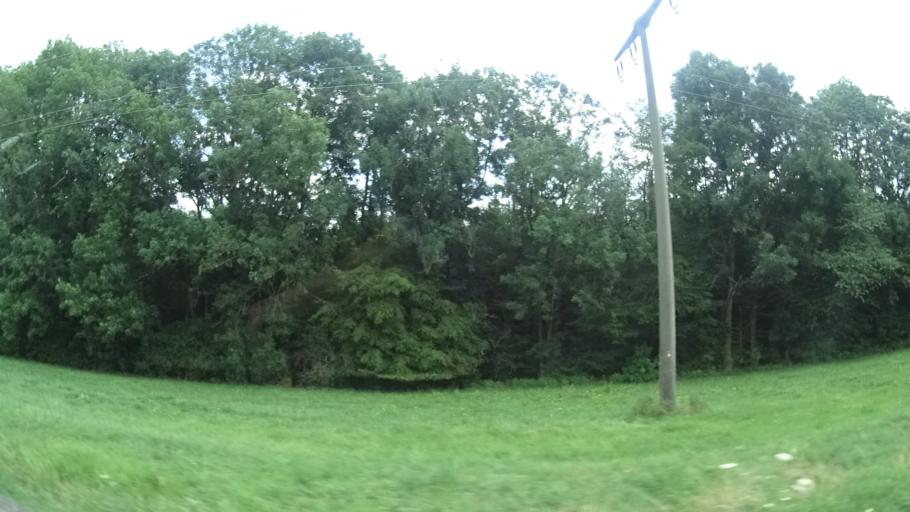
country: DE
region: Hesse
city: Gedern
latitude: 50.4294
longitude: 9.2641
